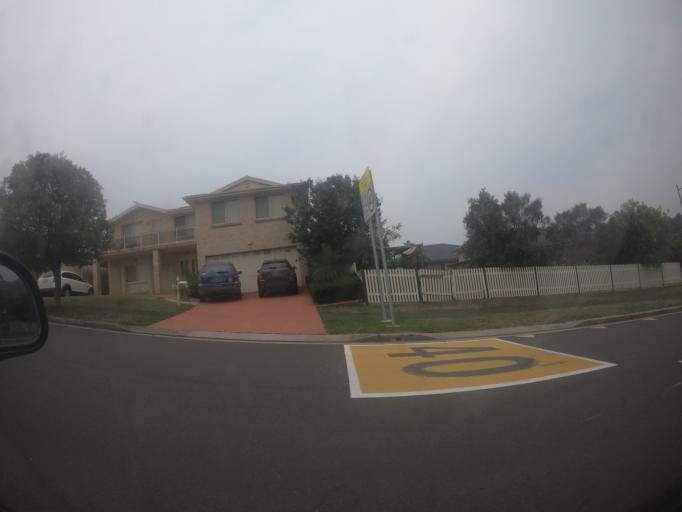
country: AU
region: New South Wales
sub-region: Shellharbour
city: Flinders
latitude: -34.5947
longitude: 150.8534
